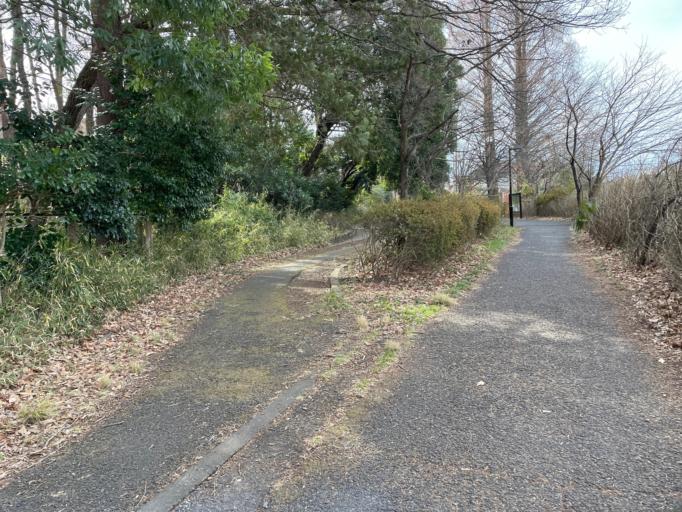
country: JP
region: Saitama
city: Tokorozawa
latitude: 35.7798
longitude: 139.5070
